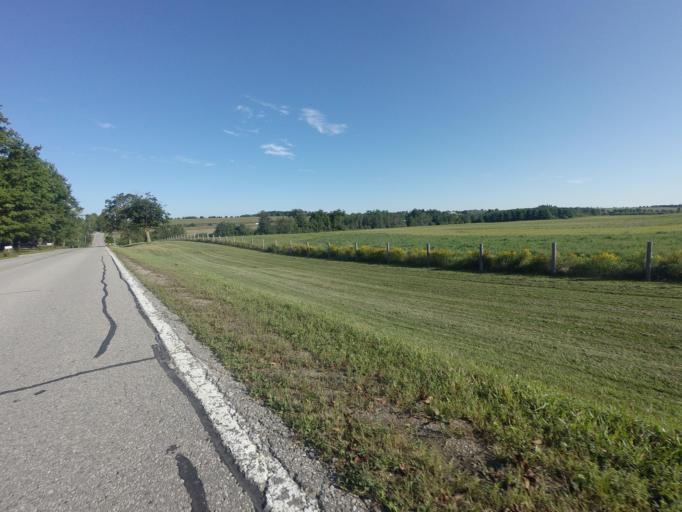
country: CA
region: Ontario
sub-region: Wellington County
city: Guelph
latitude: 43.6497
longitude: -80.4145
